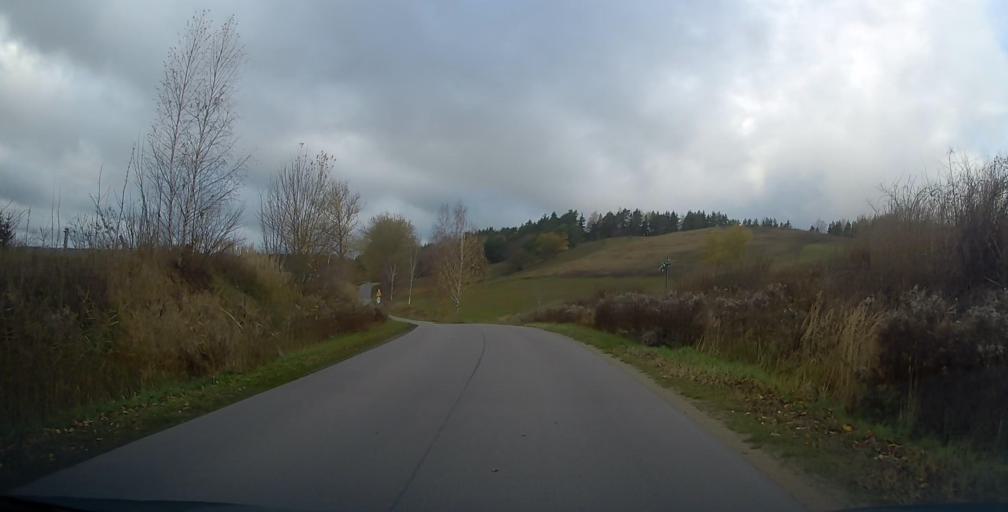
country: PL
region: Podlasie
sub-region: Suwalki
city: Suwalki
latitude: 54.2839
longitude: 22.8996
